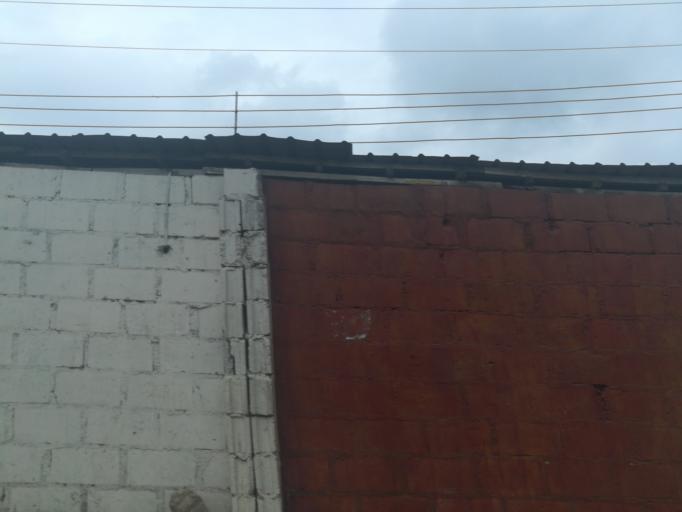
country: NG
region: Lagos
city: Ikeja
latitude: 6.6078
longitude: 3.3581
